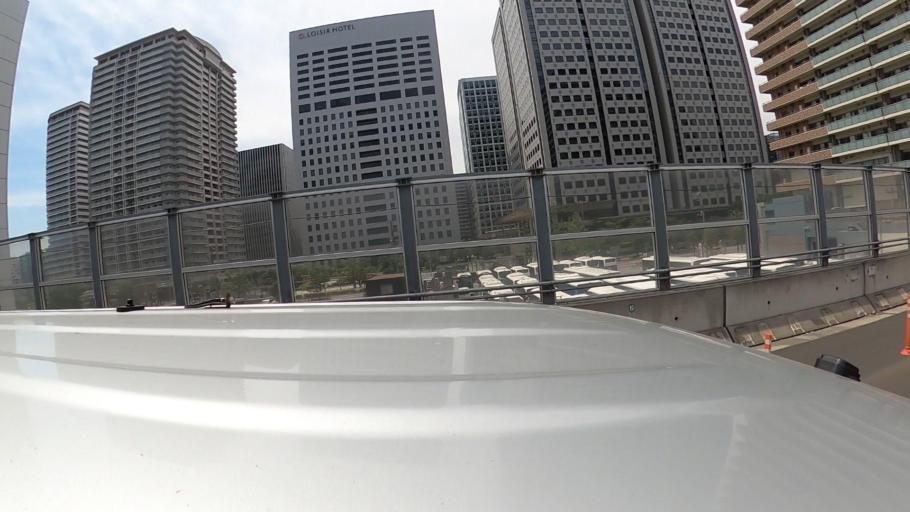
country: JP
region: Kanagawa
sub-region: Kawasaki-shi
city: Kawasaki
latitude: 35.6094
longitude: 139.7503
